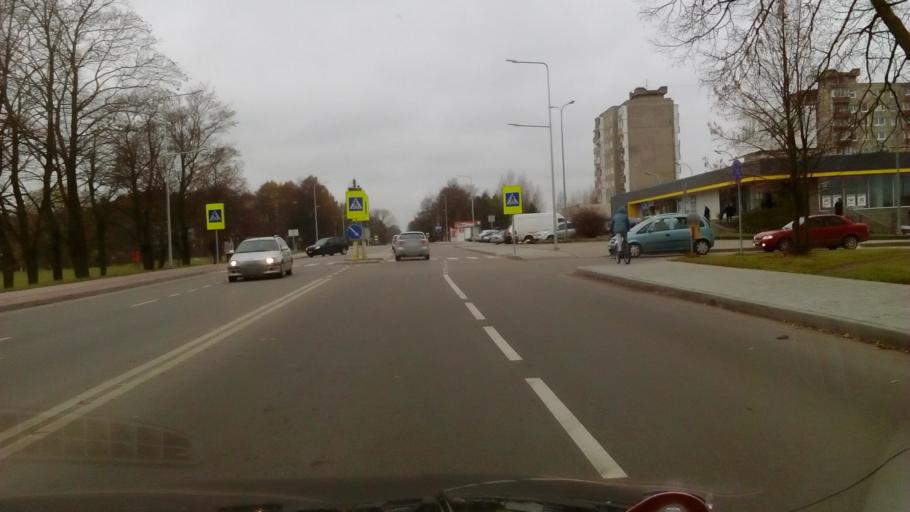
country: LT
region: Marijampoles apskritis
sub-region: Marijampole Municipality
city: Marijampole
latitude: 54.5626
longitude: 23.3339
